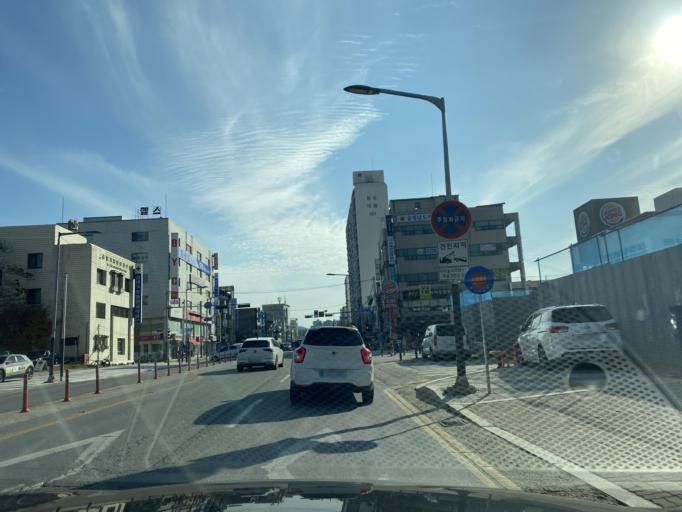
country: KR
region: Chungcheongnam-do
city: Cheonan
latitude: 36.8042
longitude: 127.1588
